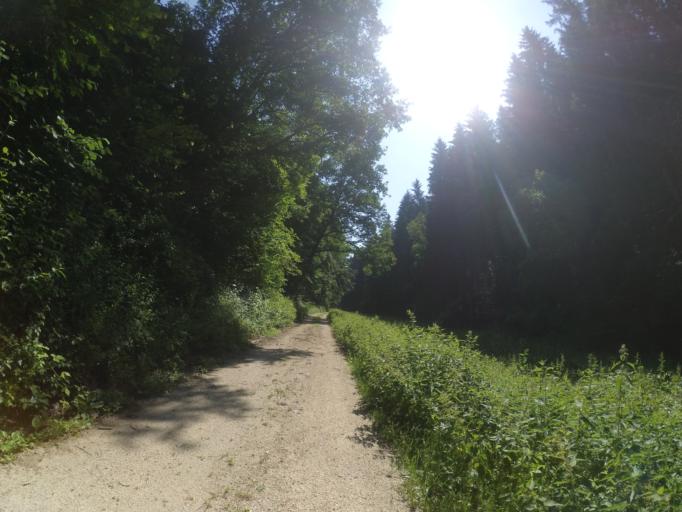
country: DE
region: Baden-Wuerttemberg
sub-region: Tuebingen Region
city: Dornstadt
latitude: 48.4473
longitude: 9.9025
